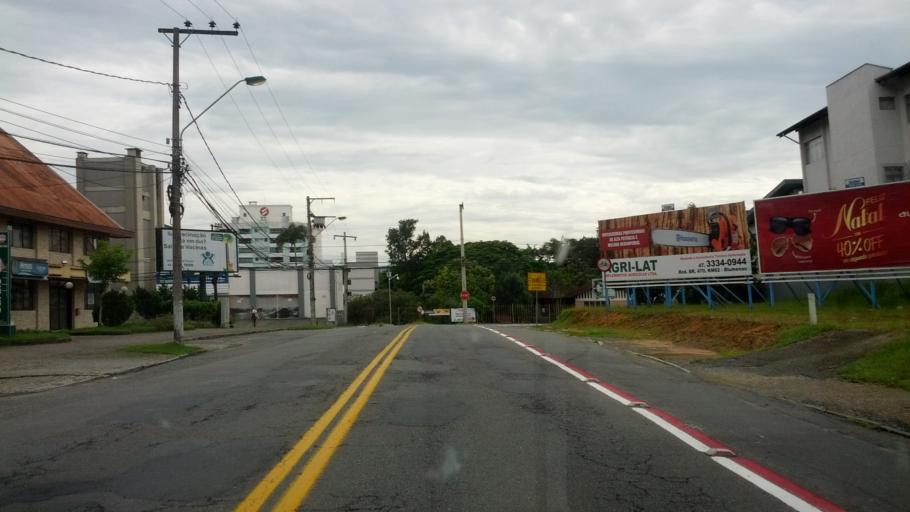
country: BR
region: Santa Catarina
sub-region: Blumenau
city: Blumenau
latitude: -26.8947
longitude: -49.0850
